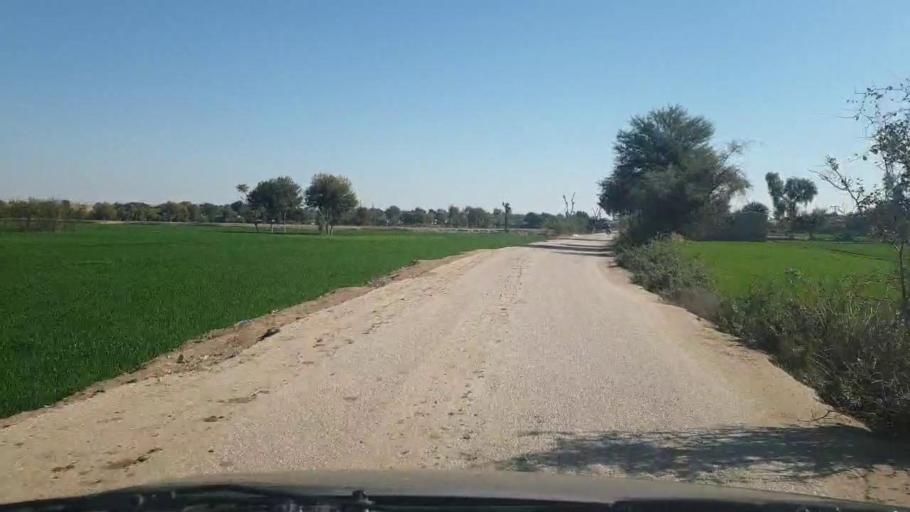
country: PK
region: Sindh
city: Bozdar
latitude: 27.0603
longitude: 68.6323
